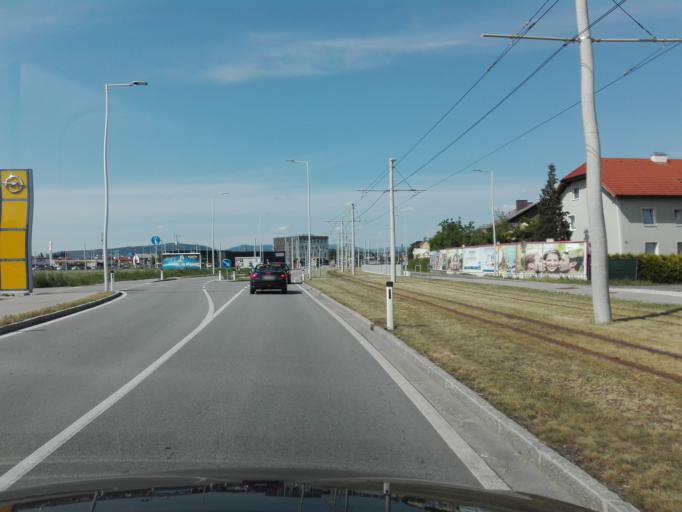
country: AT
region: Upper Austria
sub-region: Politischer Bezirk Linz-Land
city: Traun
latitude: 48.2317
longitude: 14.2343
